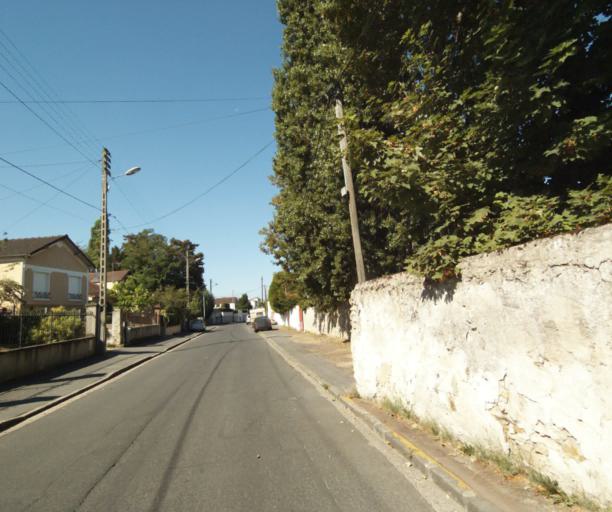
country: FR
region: Ile-de-France
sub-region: Departement de Seine-et-Marne
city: Lagny-sur-Marne
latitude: 48.8728
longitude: 2.7028
